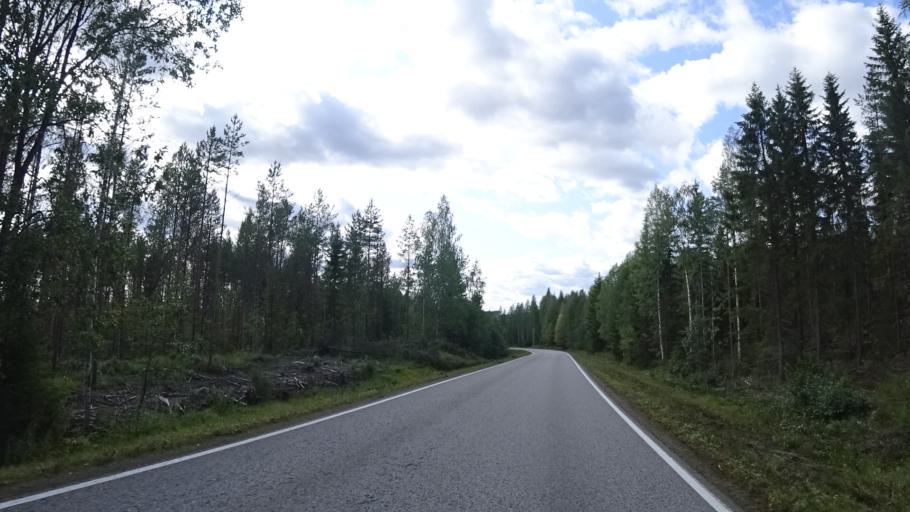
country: RU
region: Republic of Karelia
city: Vyartsilya
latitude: 62.2221
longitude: 30.6405
